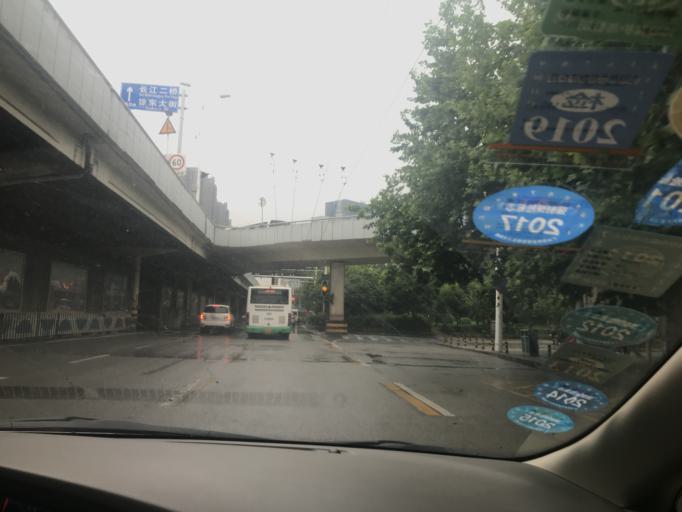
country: CN
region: Hubei
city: Jiang'an
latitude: 30.6169
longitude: 114.3052
